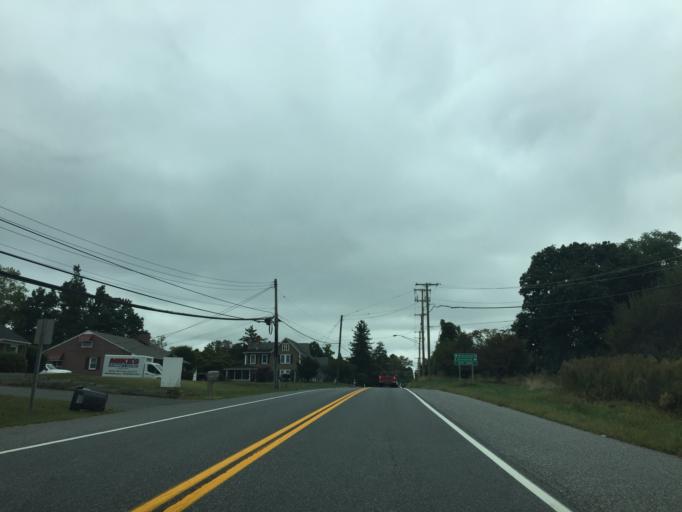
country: US
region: Maryland
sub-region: Harford County
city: Bel Air North
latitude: 39.5821
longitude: -76.3873
